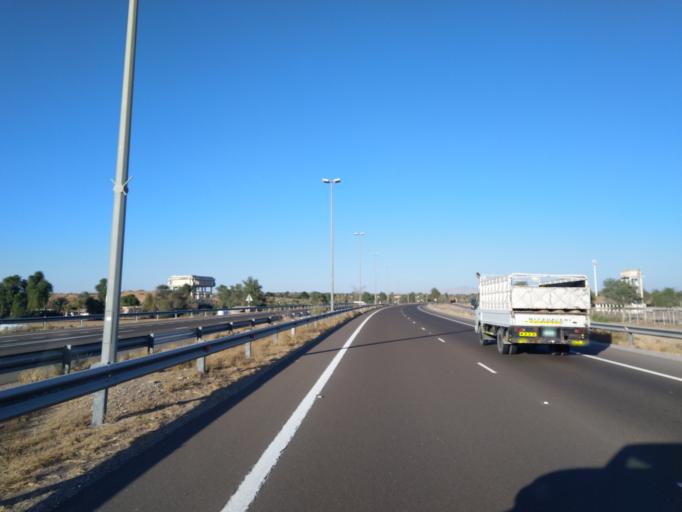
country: OM
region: Al Buraimi
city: Al Buraymi
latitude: 24.5587
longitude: 55.6936
